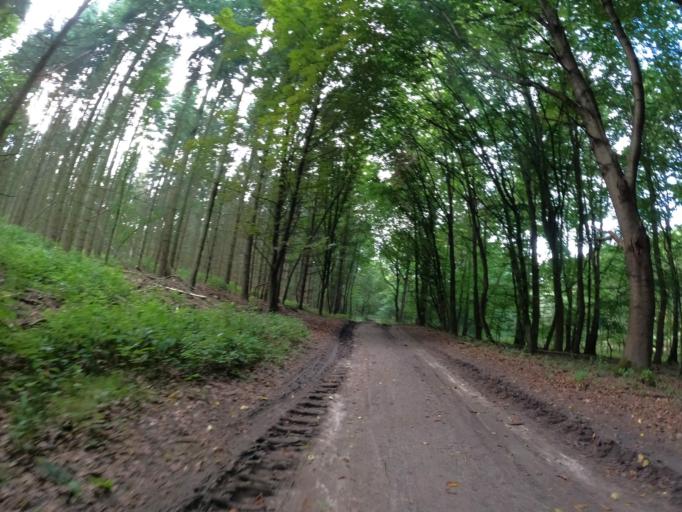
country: DE
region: Mecklenburg-Vorpommern
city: Klink
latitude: 53.4422
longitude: 12.5270
